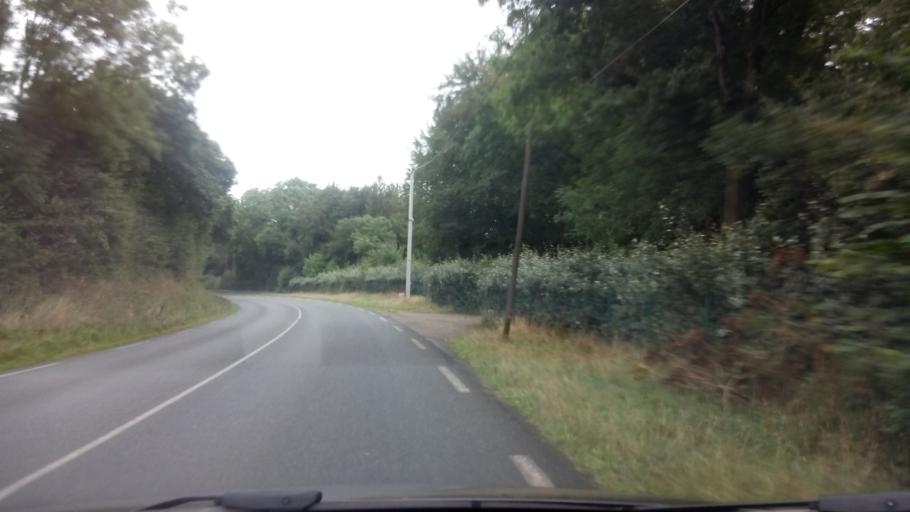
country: FR
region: Brittany
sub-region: Departement du Finistere
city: Morlaix
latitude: 48.6026
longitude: -3.8010
